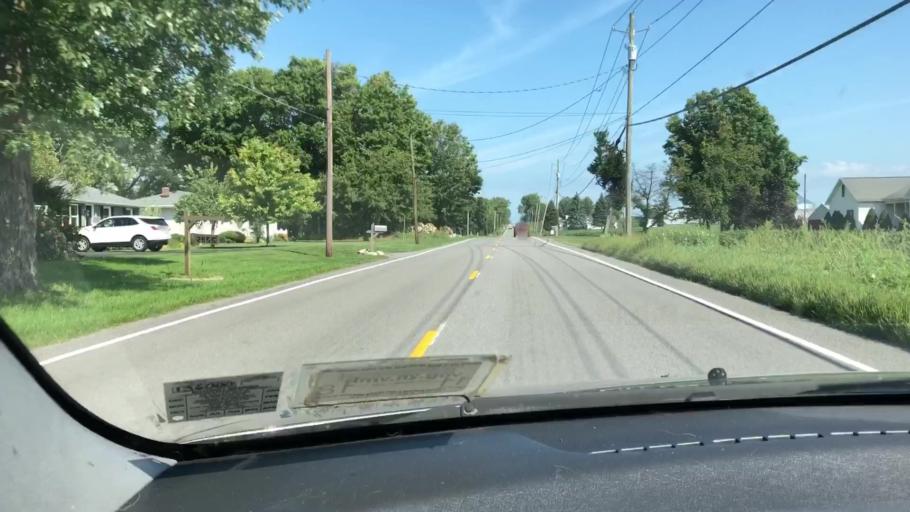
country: US
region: New York
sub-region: Wayne County
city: Macedon
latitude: 43.1020
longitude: -77.3207
